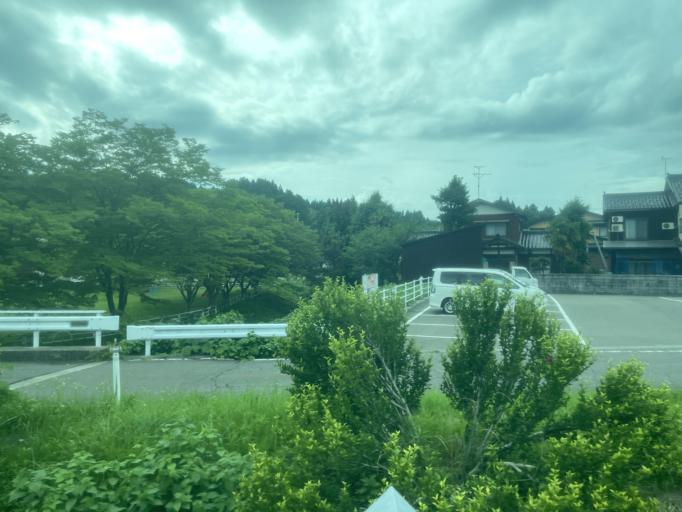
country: JP
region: Niigata
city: Nagaoka
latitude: 37.5150
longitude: 138.7036
